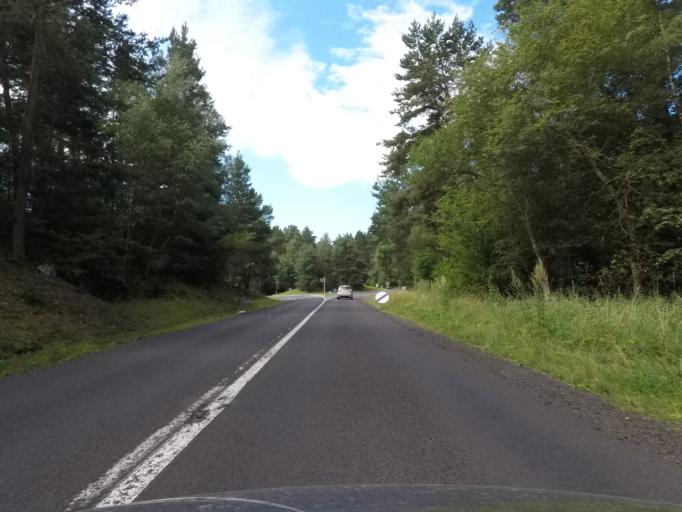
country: FR
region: Auvergne
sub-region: Departement du Puy-de-Dome
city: Aydat
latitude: 45.6747
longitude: 2.9936
